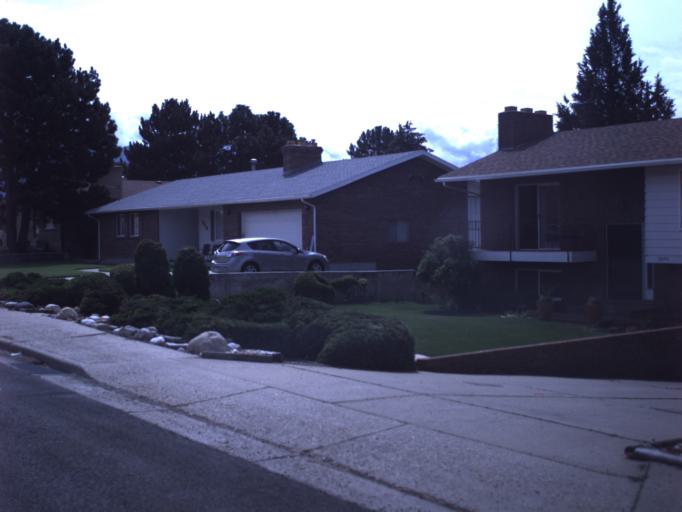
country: US
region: Utah
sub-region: Davis County
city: Hill Air Force Bace
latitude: 41.1035
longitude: -111.9935
